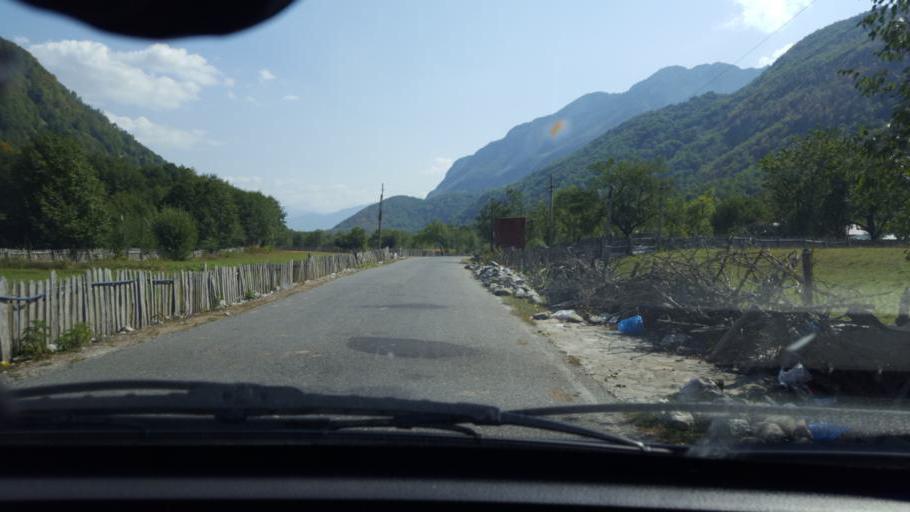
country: ME
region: Andrijevica
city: Andrijevica
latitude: 42.5859
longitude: 19.7224
